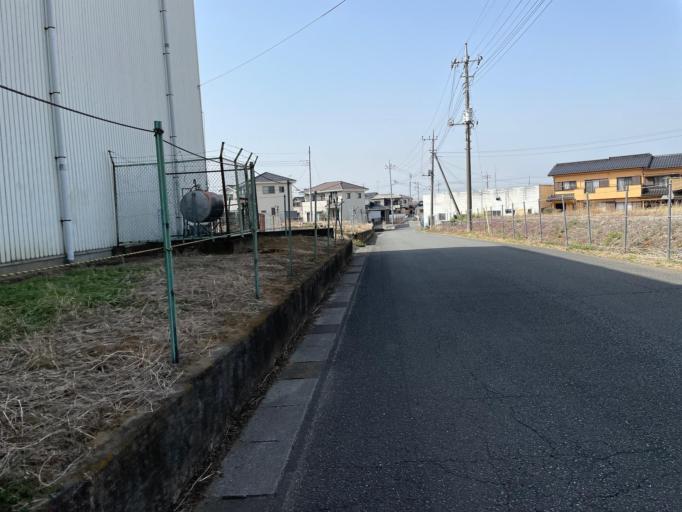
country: JP
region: Saitama
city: Ogawa
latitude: 36.1077
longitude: 139.2570
